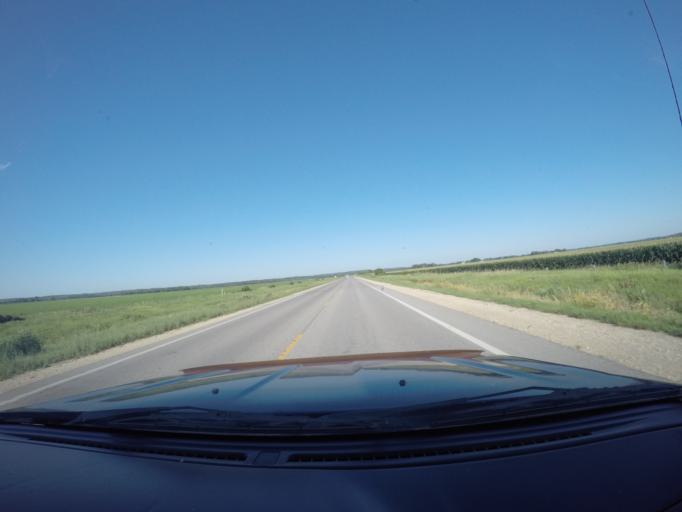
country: US
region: Kansas
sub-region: Jefferson County
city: Oskaloosa
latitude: 39.0872
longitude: -95.4381
